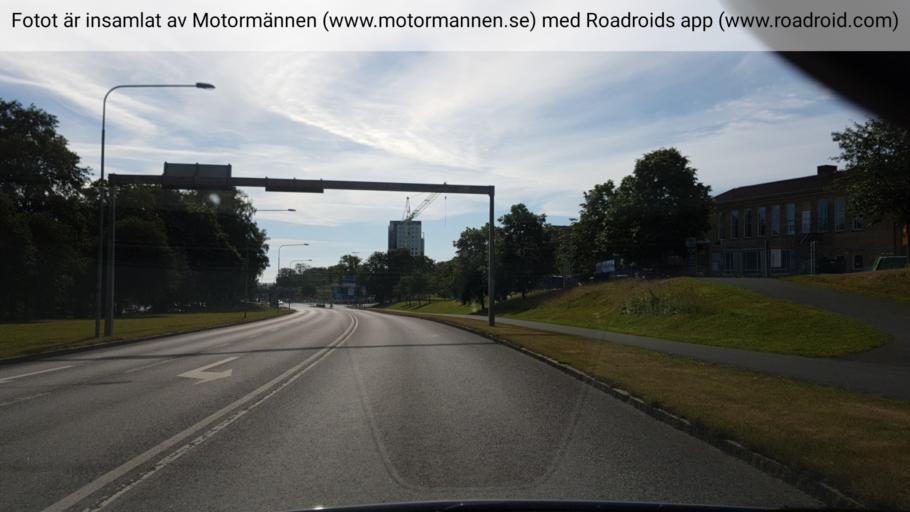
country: SE
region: Vaestra Goetaland
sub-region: Skovde Kommun
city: Skoevde
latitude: 58.3930
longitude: 13.8482
